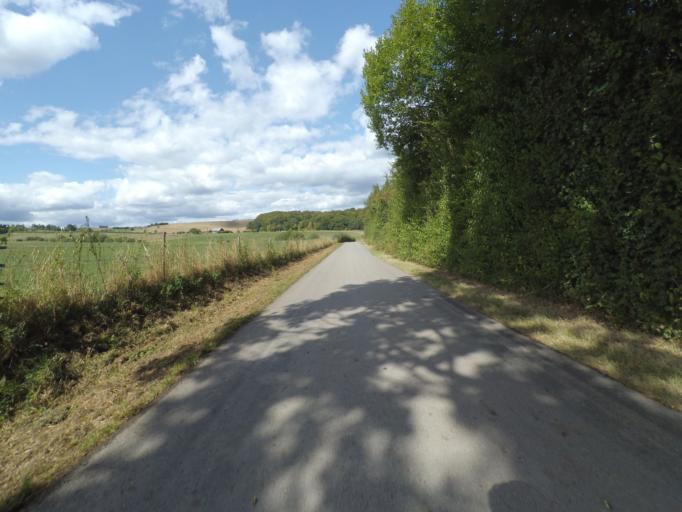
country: LU
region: Grevenmacher
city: Gonderange
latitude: 49.6817
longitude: 6.2664
